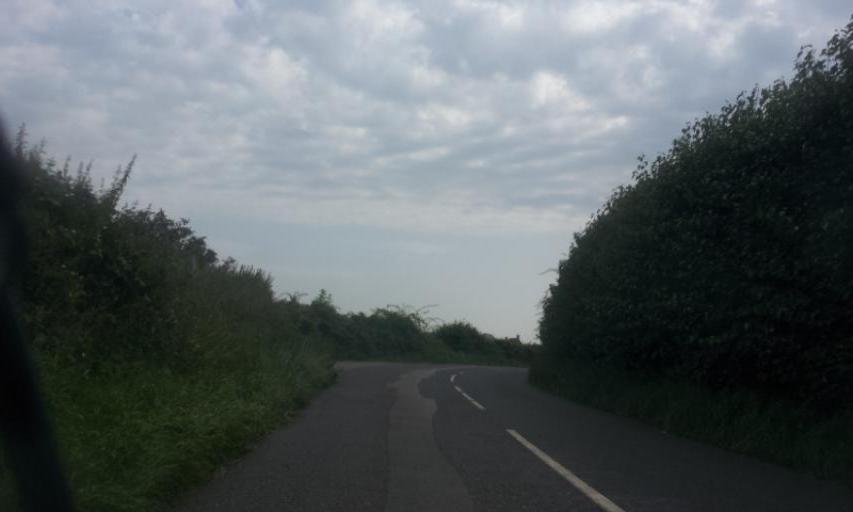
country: GB
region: England
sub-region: Kent
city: Aylesford
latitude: 51.2884
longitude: 0.4572
